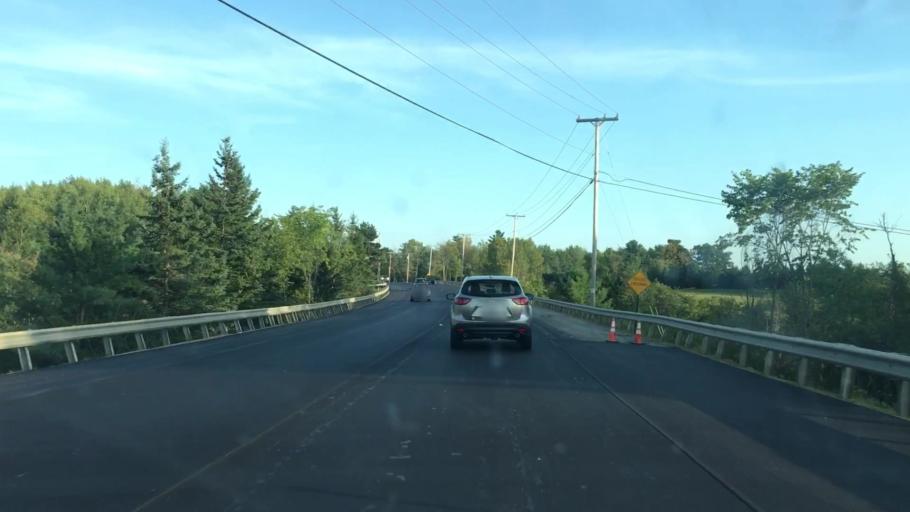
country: US
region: Maine
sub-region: Penobscot County
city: Hampden
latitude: 44.7688
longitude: -68.8561
